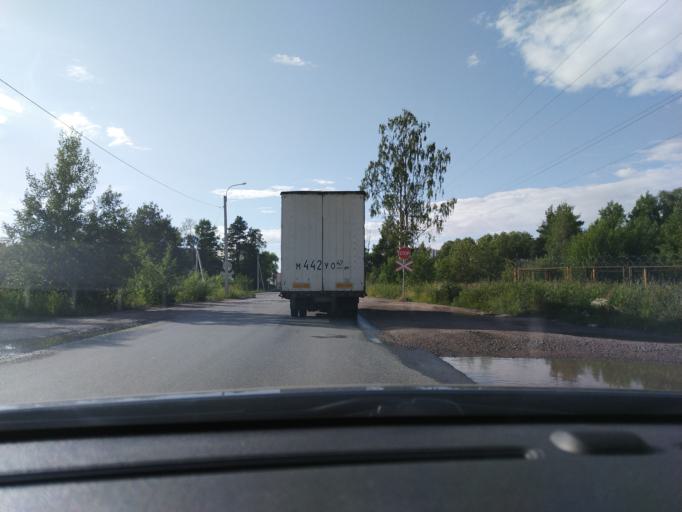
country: RU
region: St.-Petersburg
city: Gorelovo
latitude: 59.7837
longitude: 30.1699
